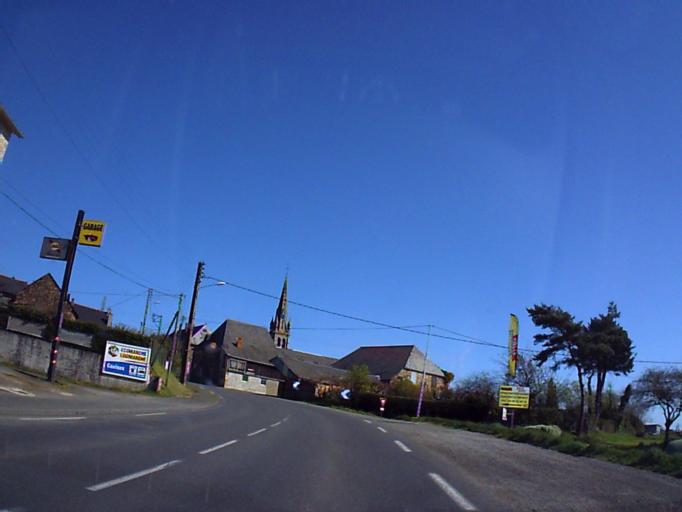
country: FR
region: Brittany
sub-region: Departement des Cotes-d'Armor
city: Caulnes
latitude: 48.2660
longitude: -2.1601
